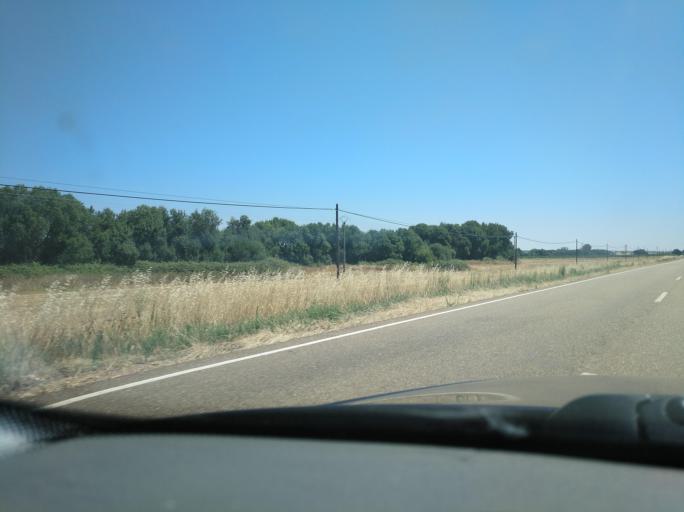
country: ES
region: Extremadura
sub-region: Provincia de Badajoz
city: Olivenza
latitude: 38.7061
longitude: -7.1759
